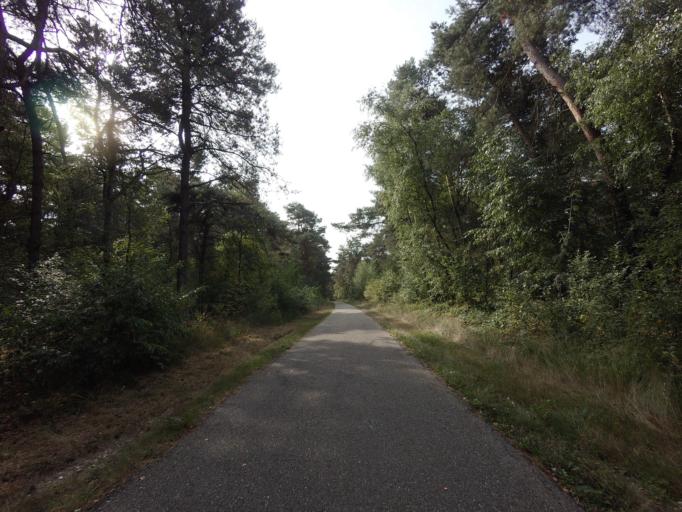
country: NL
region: North Brabant
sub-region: Gemeente Mill en Sint Hubert
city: Wilbertoord
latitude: 51.6151
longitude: 5.8163
